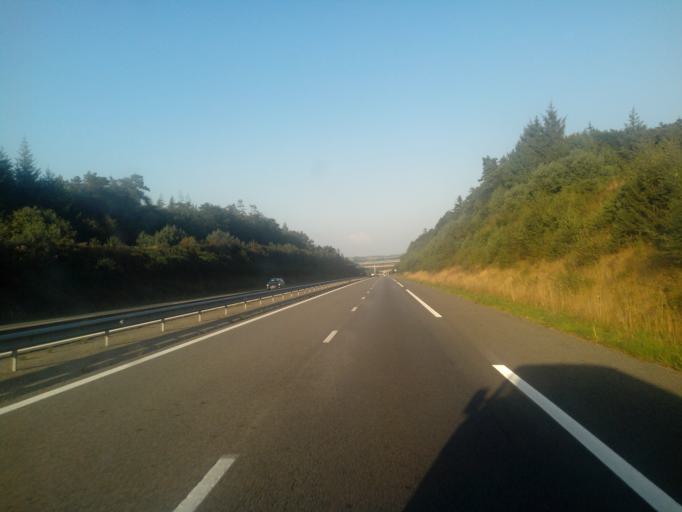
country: FR
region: Brittany
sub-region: Departement du Morbihan
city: Saint-Gonnery
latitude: 48.1297
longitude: -2.8246
